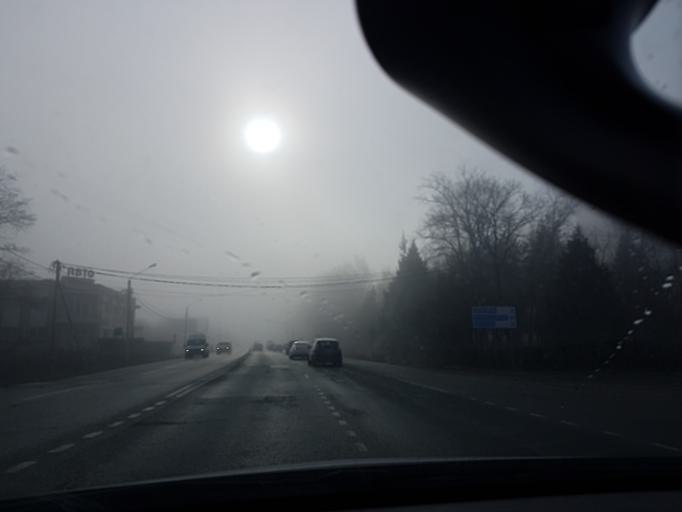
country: RU
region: Moskovskaya
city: Istra
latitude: 55.9059
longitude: 36.8870
